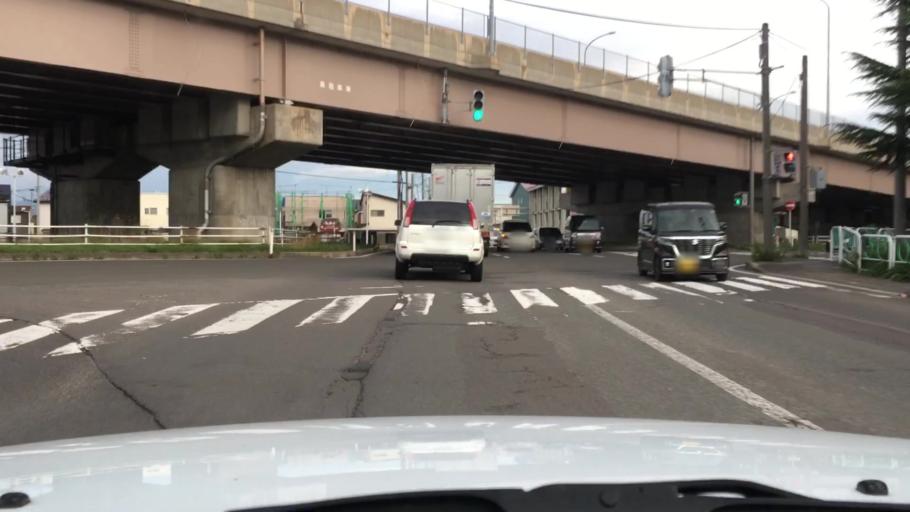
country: JP
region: Aomori
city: Hirosaki
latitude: 40.5957
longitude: 140.5034
